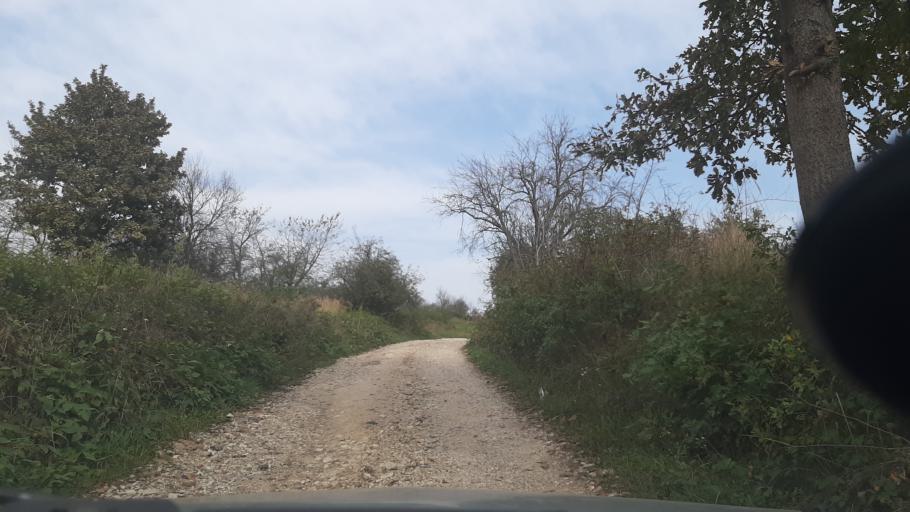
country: BA
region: Republika Srpska
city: Maglajani
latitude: 44.8746
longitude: 17.4719
